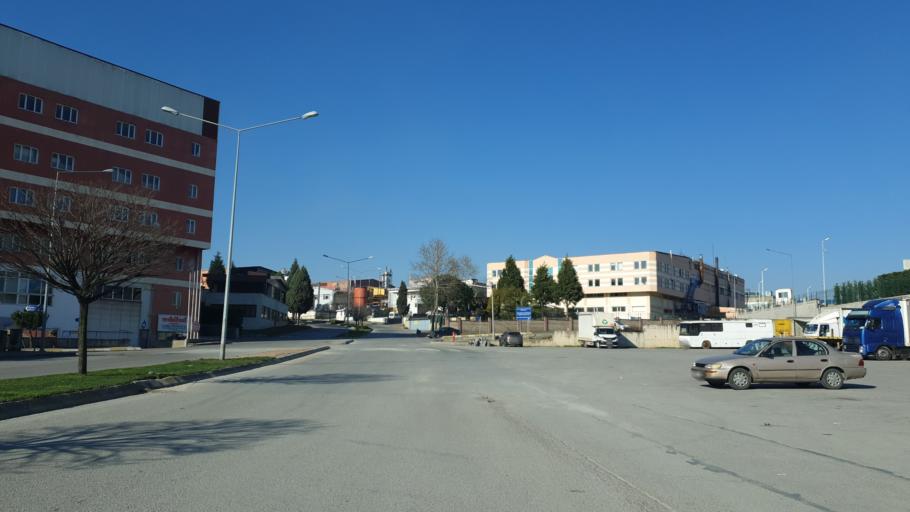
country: TR
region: Kocaeli
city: Balcik
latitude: 40.8784
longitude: 29.3714
